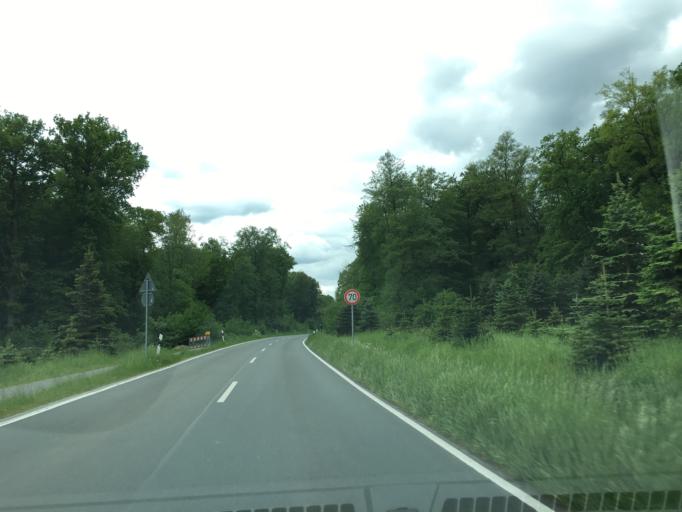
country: DE
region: North Rhine-Westphalia
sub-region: Regierungsbezirk Munster
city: Muenster
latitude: 51.9119
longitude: 7.5713
